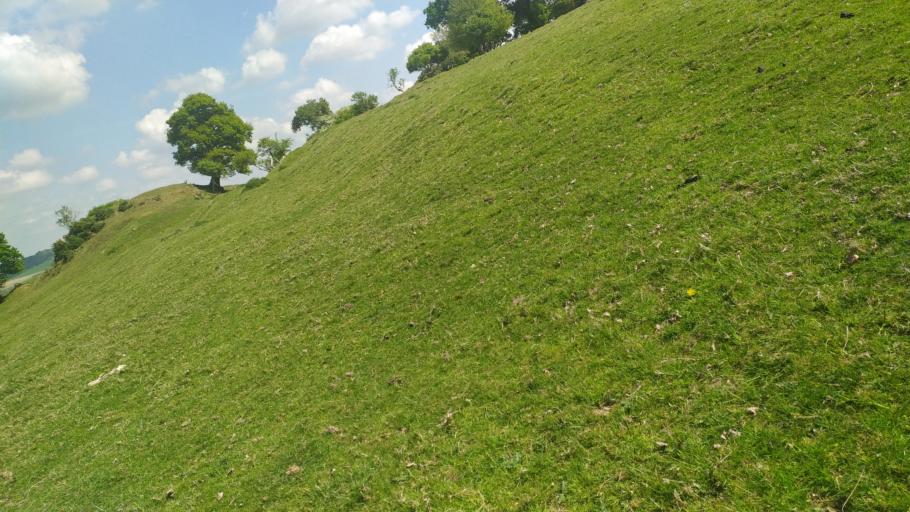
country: GB
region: England
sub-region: North Yorkshire
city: Pannal
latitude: 53.9016
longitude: -1.5293
